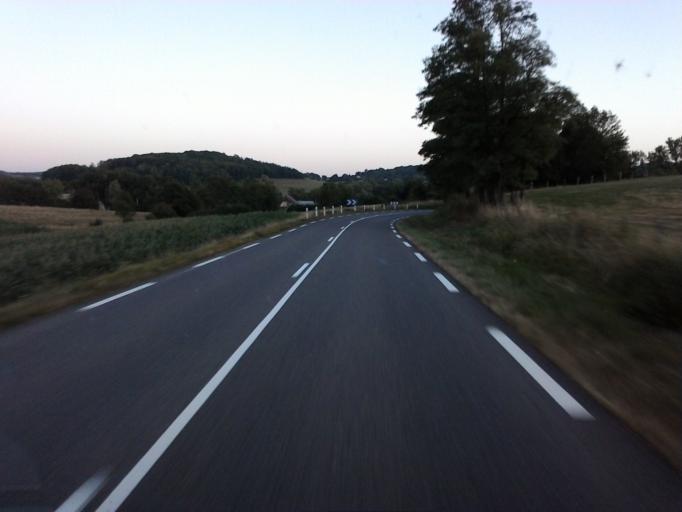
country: FR
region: Franche-Comte
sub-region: Departement du Jura
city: Poligny
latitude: 46.8180
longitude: 5.5931
